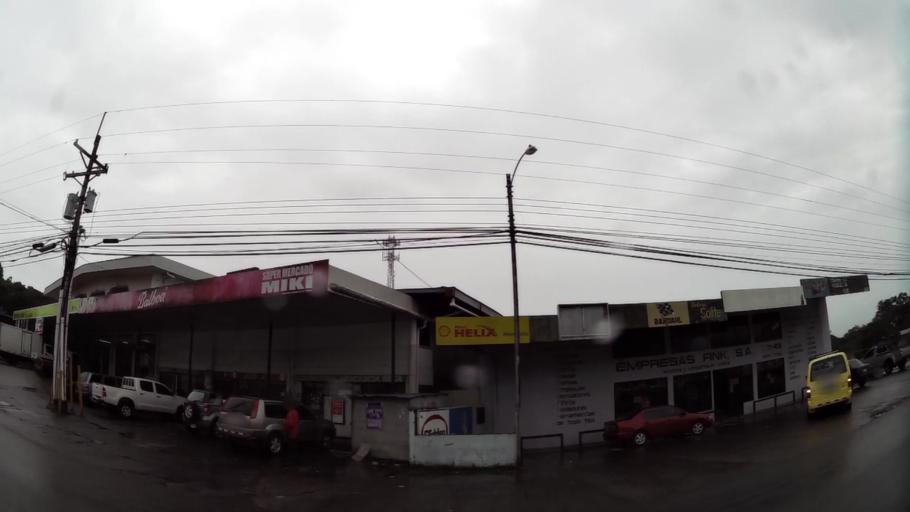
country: PA
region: Chiriqui
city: Volcan
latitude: 8.7767
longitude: -82.6419
